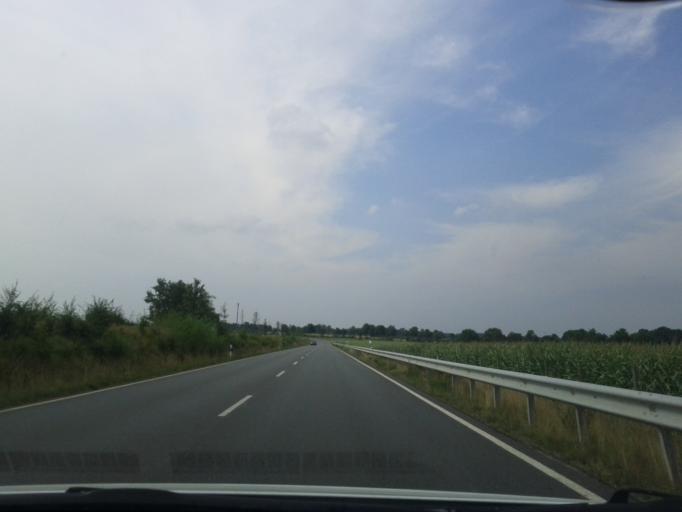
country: DE
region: Lower Saxony
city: Agathenburg
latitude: 53.5577
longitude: 9.5021
